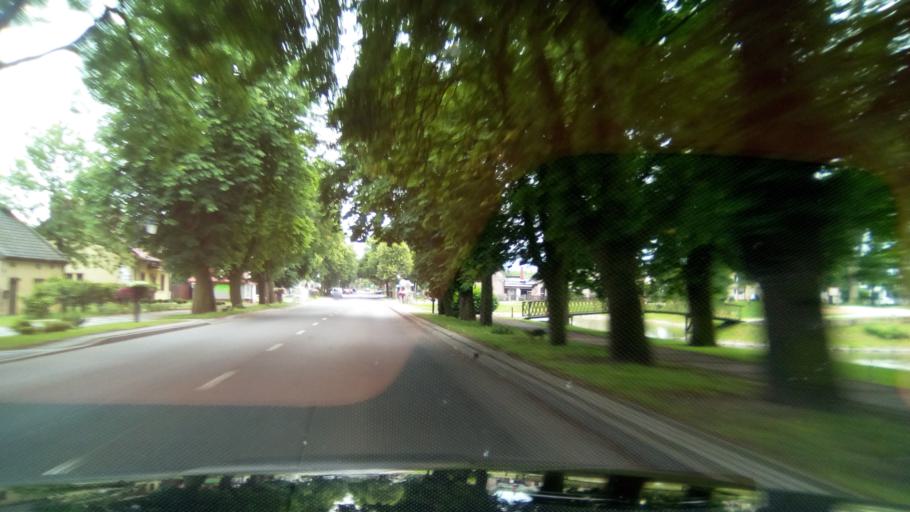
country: PL
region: Greater Poland Voivodeship
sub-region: Powiat gnieznienski
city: Czerniejewo
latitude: 52.4308
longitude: 17.4893
